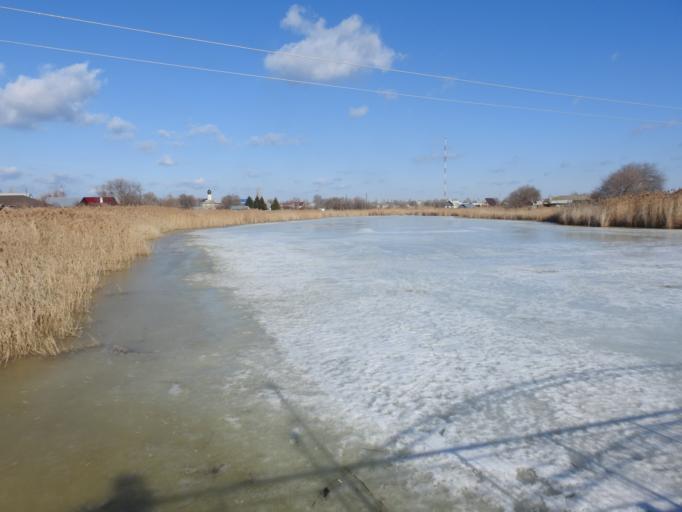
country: RU
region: Saratov
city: Yershov
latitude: 51.3547
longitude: 48.2679
